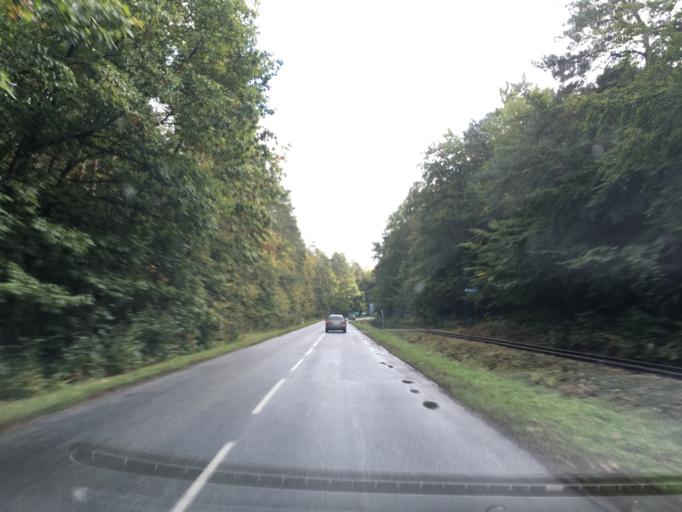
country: PL
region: Pomeranian Voivodeship
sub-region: Powiat nowodworski
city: Stegna
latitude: 54.3348
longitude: 19.0086
